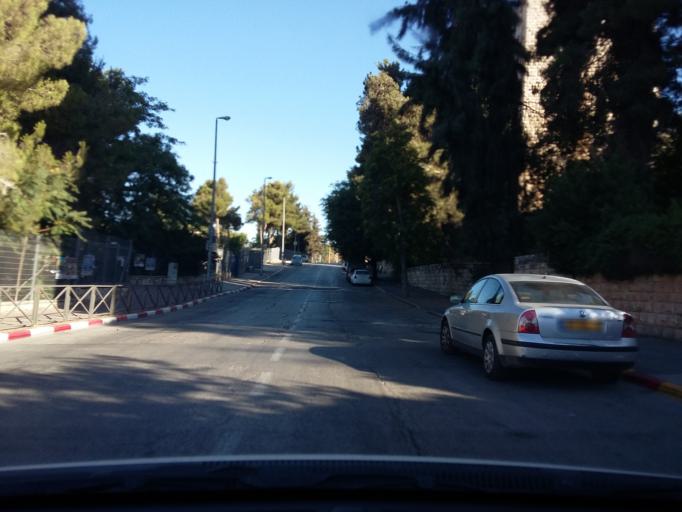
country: PS
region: West Bank
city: East Jerusalem
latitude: 31.8023
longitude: 35.2395
